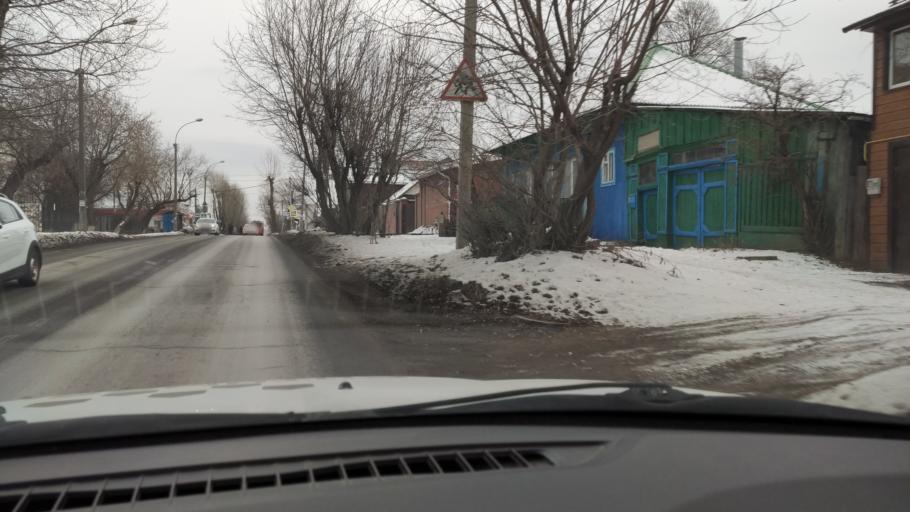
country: RU
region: Perm
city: Perm
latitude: 58.0374
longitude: 56.3311
